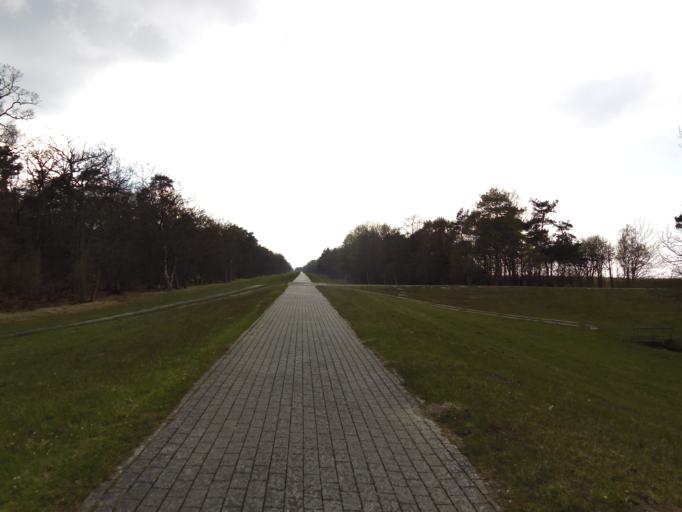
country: DE
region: Mecklenburg-Vorpommern
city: Zingst
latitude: 54.4408
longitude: 12.7567
